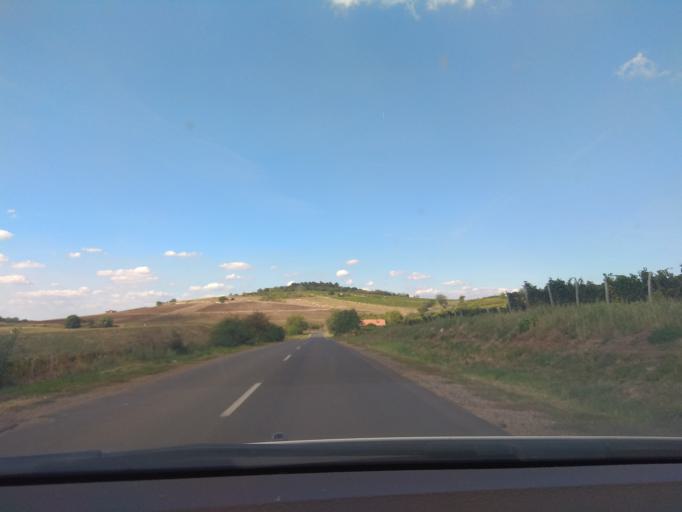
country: HU
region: Borsod-Abauj-Zemplen
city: Mad
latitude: 48.1974
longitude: 21.2591
